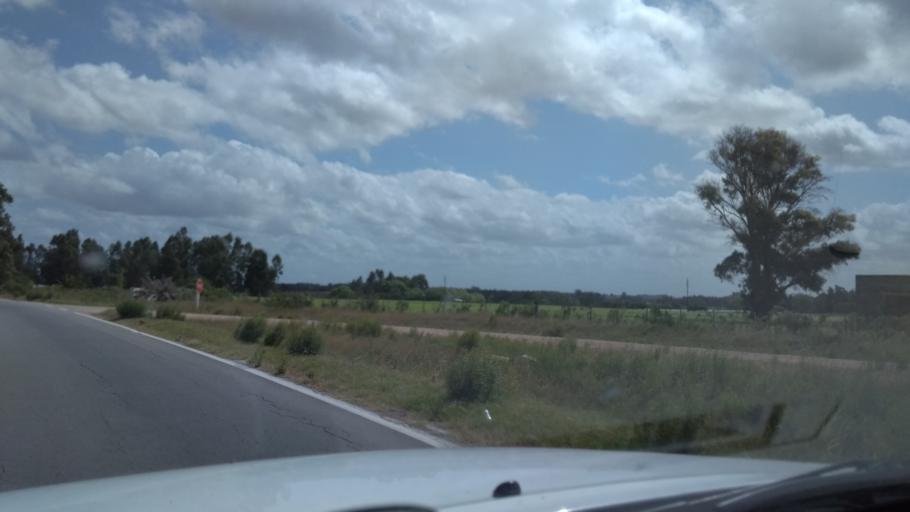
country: UY
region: Canelones
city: San Bautista
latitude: -34.4618
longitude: -56.0037
